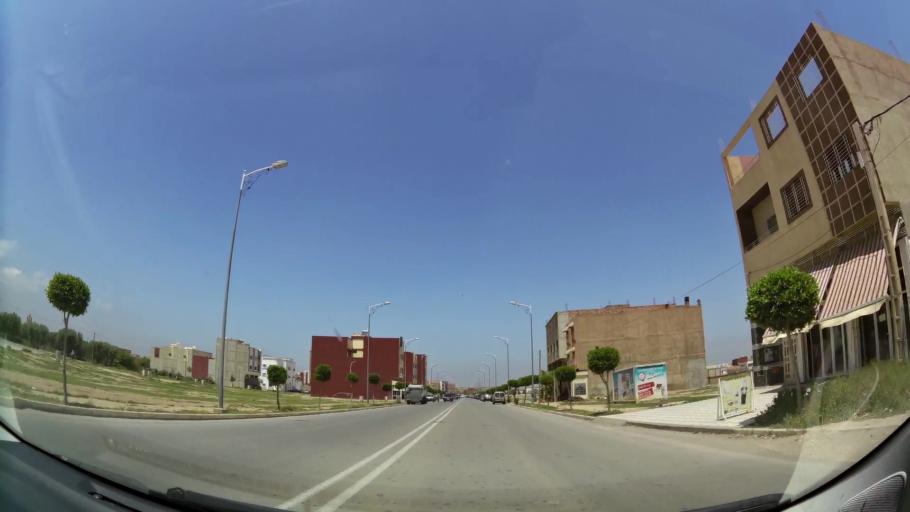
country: MA
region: Oriental
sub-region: Oujda-Angad
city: Oujda
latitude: 34.6934
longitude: -1.8922
